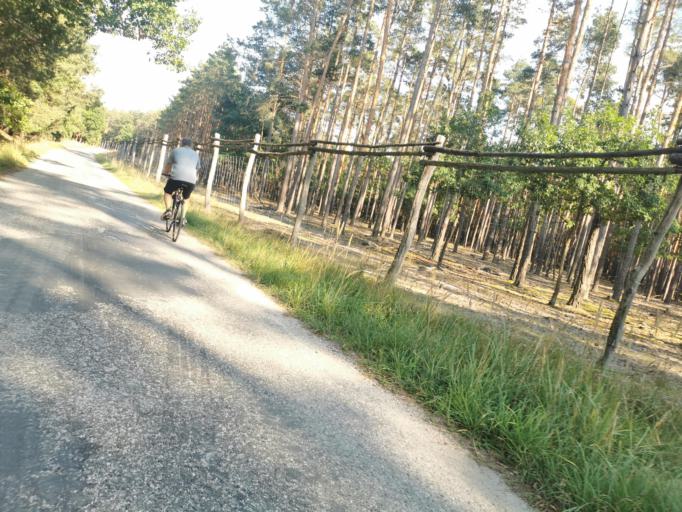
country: SK
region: Trnavsky
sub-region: Okres Senica
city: Senica
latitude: 48.6352
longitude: 17.2936
